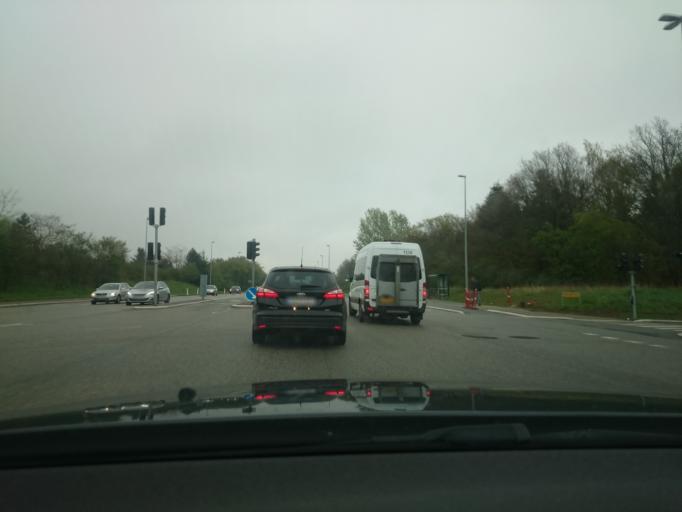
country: DK
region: Capital Region
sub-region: Ballerup Kommune
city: Ballerup
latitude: 55.7489
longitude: 12.3991
